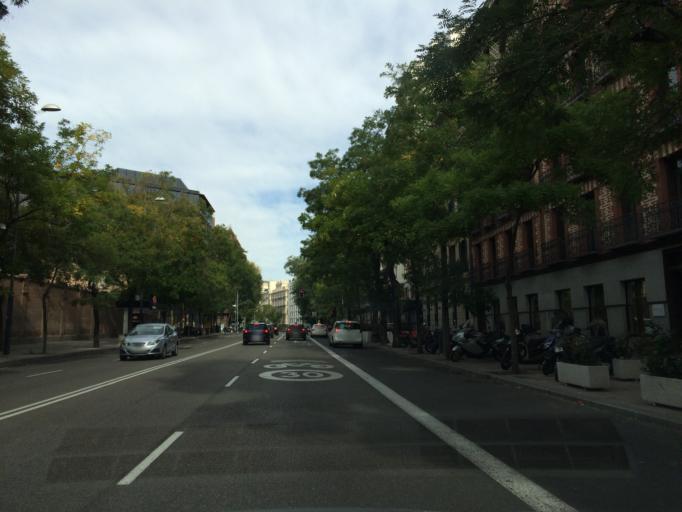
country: ES
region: Madrid
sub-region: Provincia de Madrid
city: Chamberi
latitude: 40.4288
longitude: -3.6945
